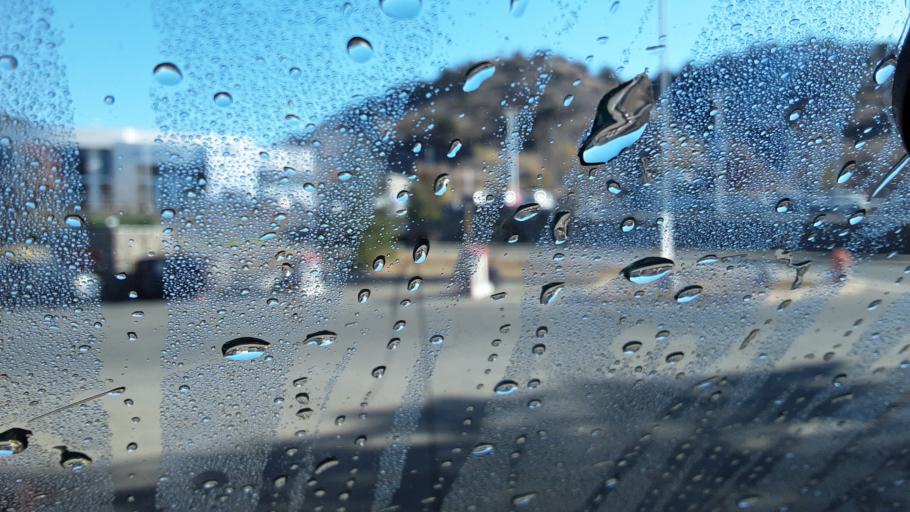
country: US
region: Colorado
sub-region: La Plata County
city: Durango
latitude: 37.2294
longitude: -107.8608
